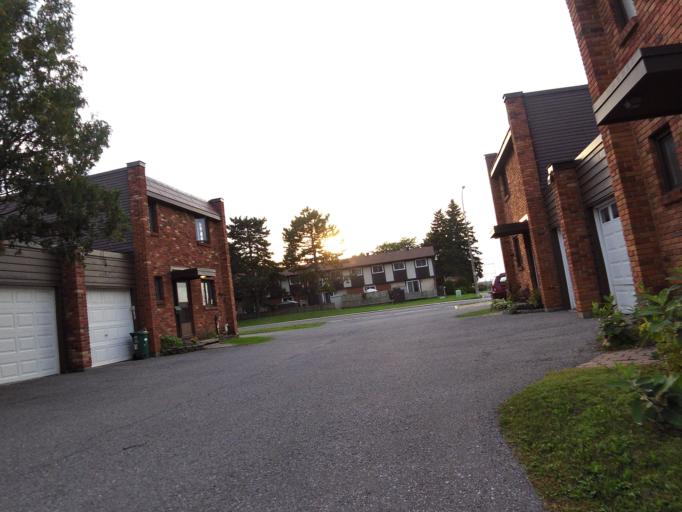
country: CA
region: Ontario
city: Bells Corners
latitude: 45.3179
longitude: -75.8266
